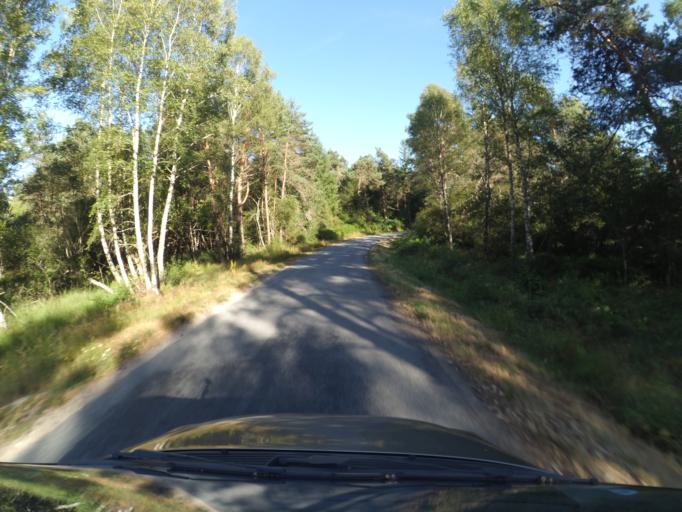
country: FR
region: Limousin
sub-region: Departement de la Creuse
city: Banize
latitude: 45.7903
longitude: 1.9555
